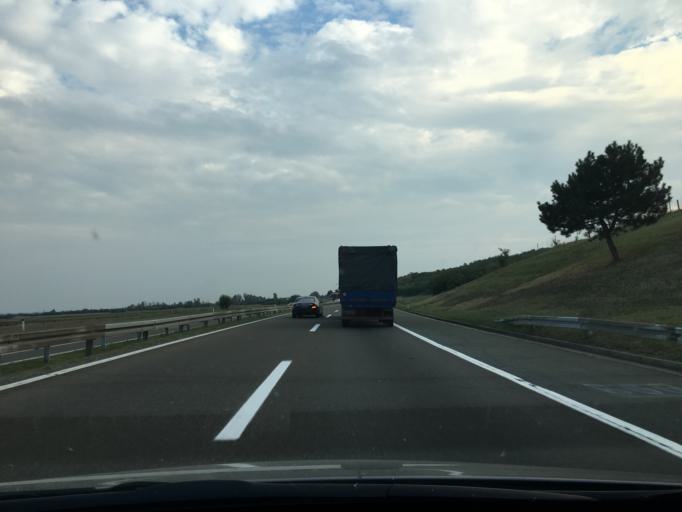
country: RS
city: Lugavcina
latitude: 44.4521
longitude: 21.0451
